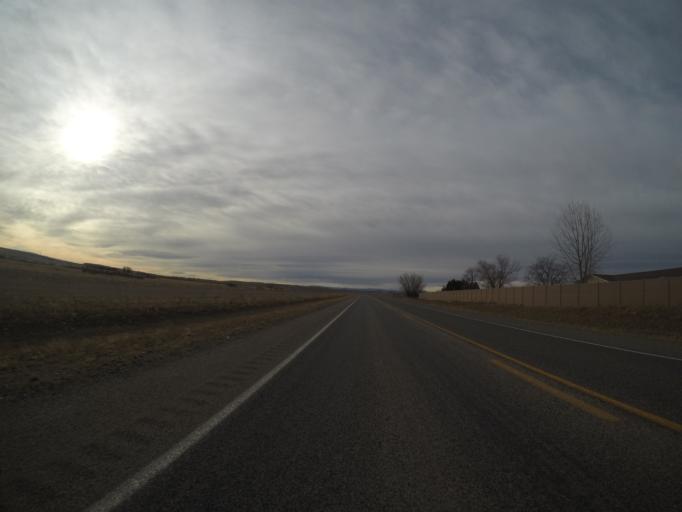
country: US
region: Montana
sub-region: Yellowstone County
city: Laurel
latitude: 45.6185
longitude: -108.8138
